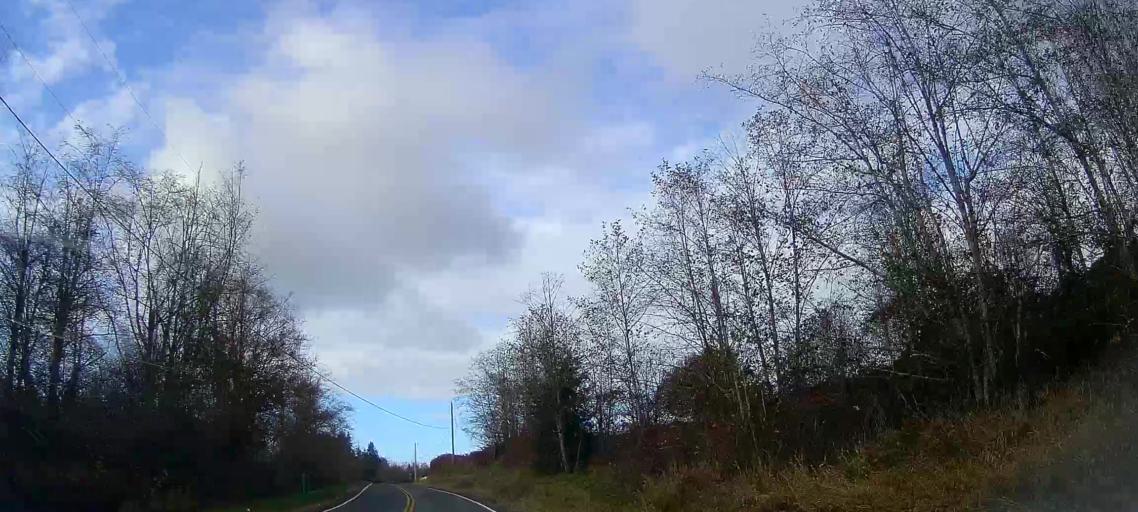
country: US
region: Washington
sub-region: Skagit County
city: Big Lake
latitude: 48.4100
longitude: -122.2190
